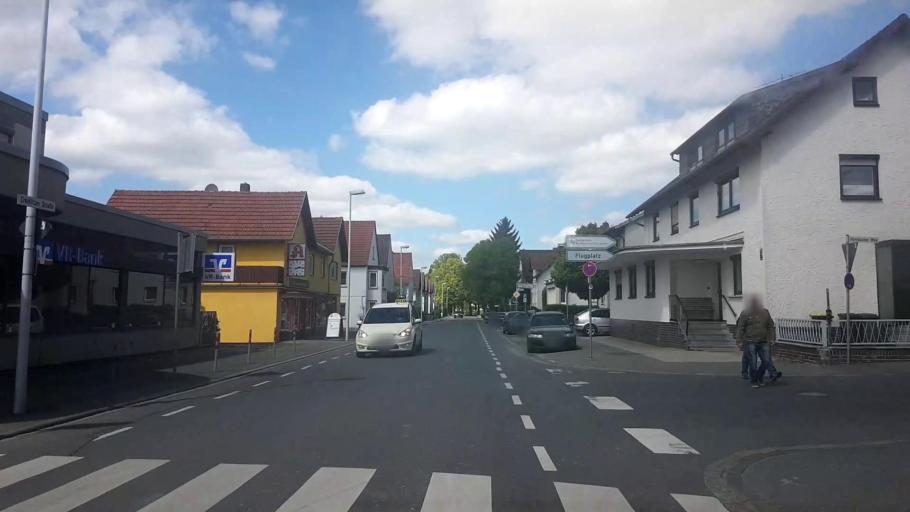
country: DE
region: Bavaria
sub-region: Upper Franconia
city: Niederfullbach
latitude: 50.2357
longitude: 10.9786
